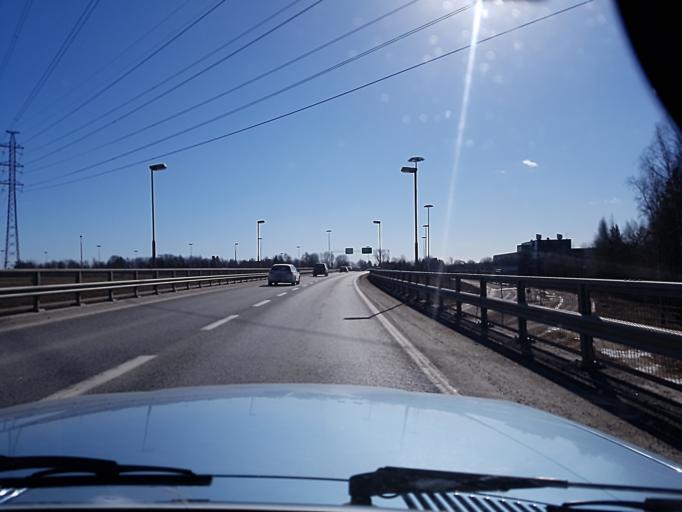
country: FI
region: Uusimaa
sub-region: Helsinki
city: Vantaa
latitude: 60.2882
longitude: 24.9764
